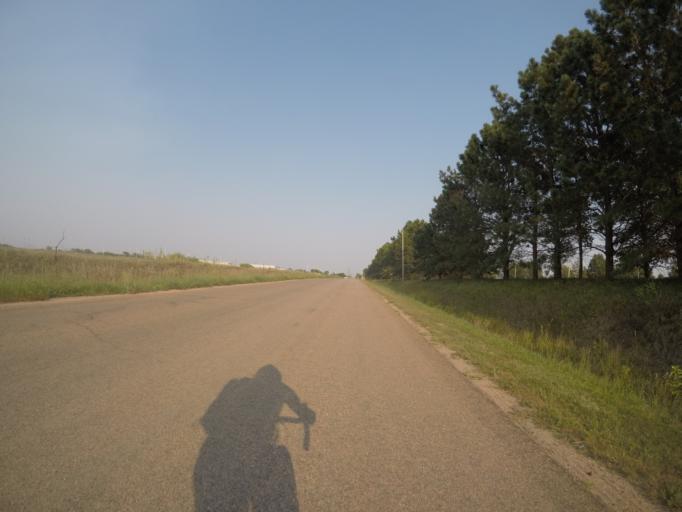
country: US
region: Nebraska
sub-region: Gage County
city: Beatrice
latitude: 40.2629
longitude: -96.7898
